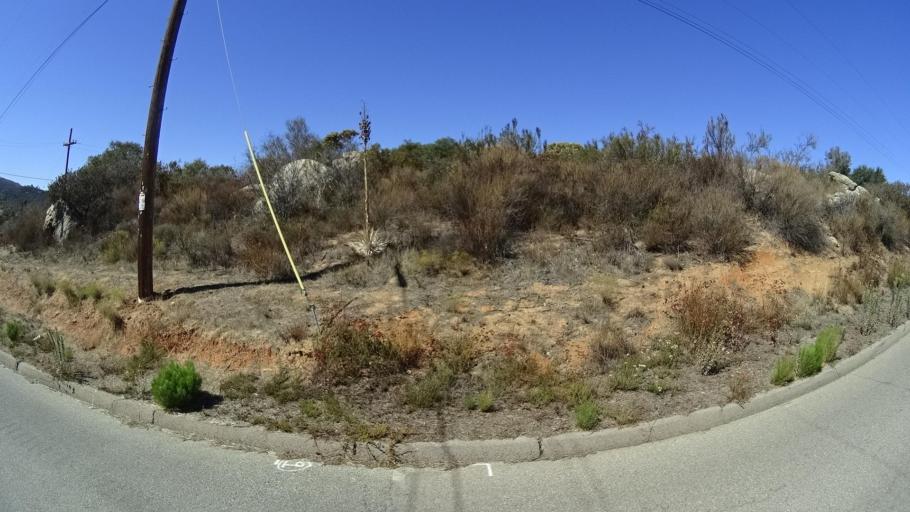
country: US
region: California
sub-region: San Diego County
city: Alpine
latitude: 32.7570
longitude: -116.7706
